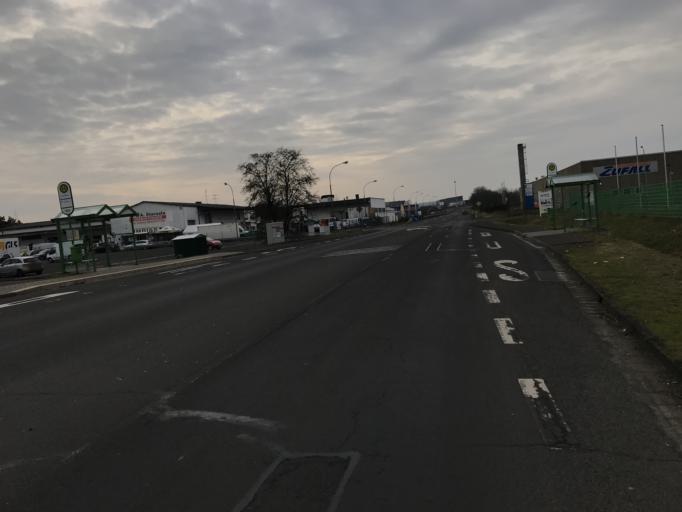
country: DE
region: Hesse
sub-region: Regierungsbezirk Giessen
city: Grossen Buseck
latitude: 50.5874
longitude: 8.7646
